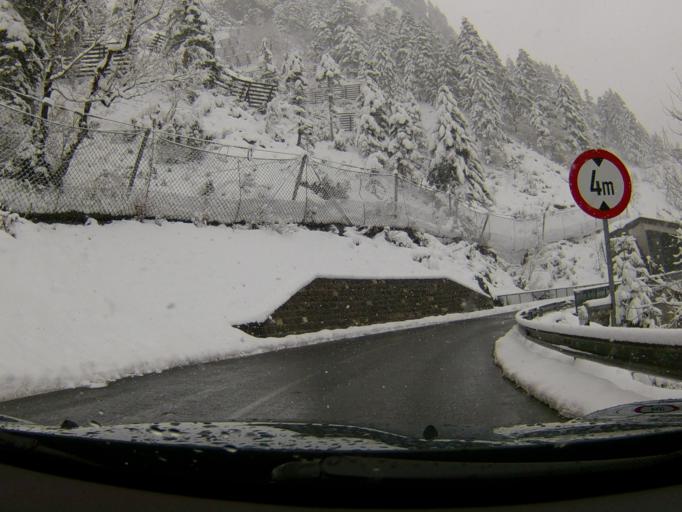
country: AT
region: Vorarlberg
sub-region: Politischer Bezirk Bregenz
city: Schroecken
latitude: 47.2684
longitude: 10.0655
